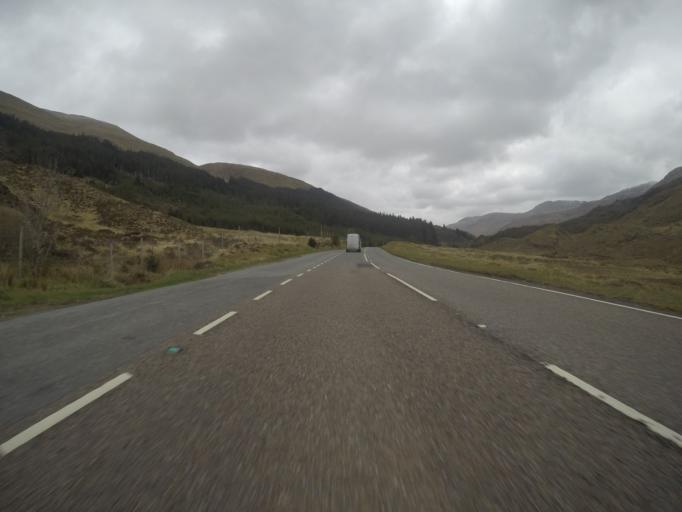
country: GB
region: Scotland
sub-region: Highland
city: Fort William
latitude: 57.1663
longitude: -5.2810
